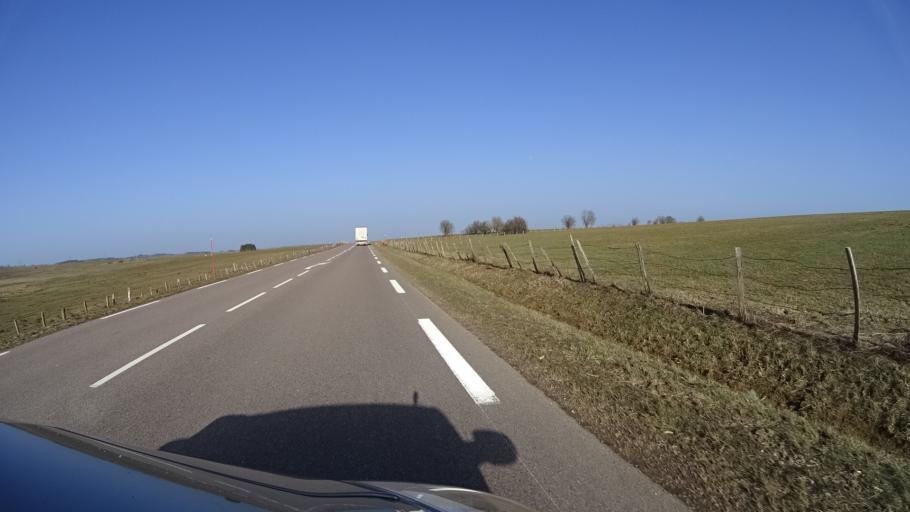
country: FR
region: Franche-Comte
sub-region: Departement du Doubs
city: Frasne
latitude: 46.8802
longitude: 6.1983
